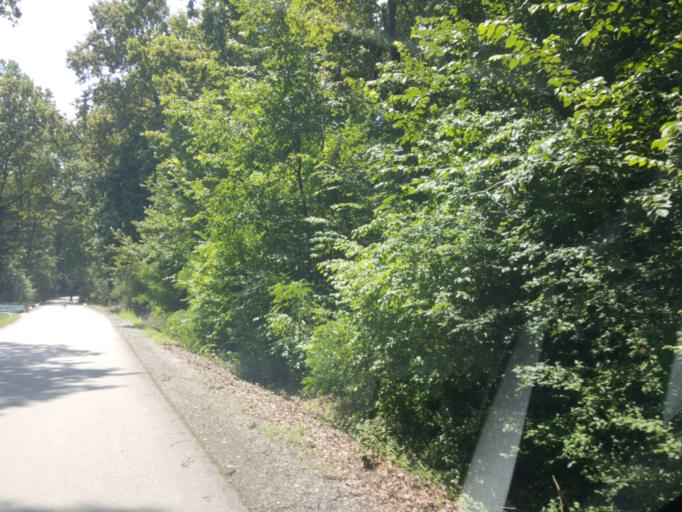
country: RS
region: Autonomna Pokrajina Vojvodina
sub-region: Sremski Okrug
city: Sid
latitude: 45.0386
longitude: 19.1384
